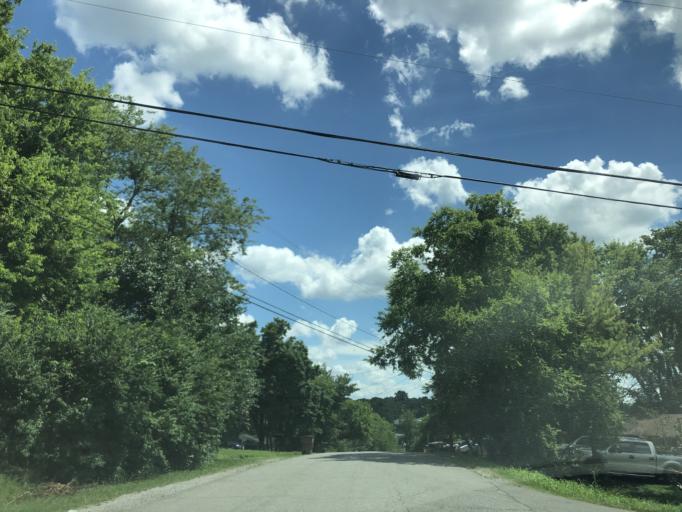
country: US
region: Tennessee
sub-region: Davidson County
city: Oak Hill
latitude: 36.0726
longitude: -86.7204
